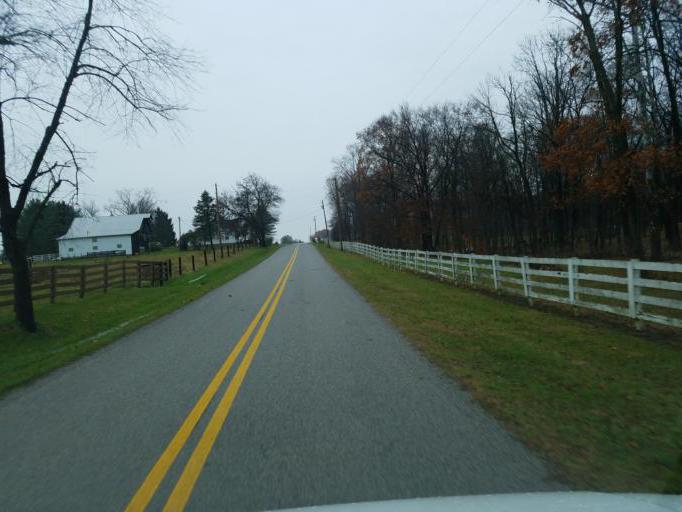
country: US
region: Ohio
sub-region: Knox County
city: Centerburg
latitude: 40.3298
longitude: -82.7762
